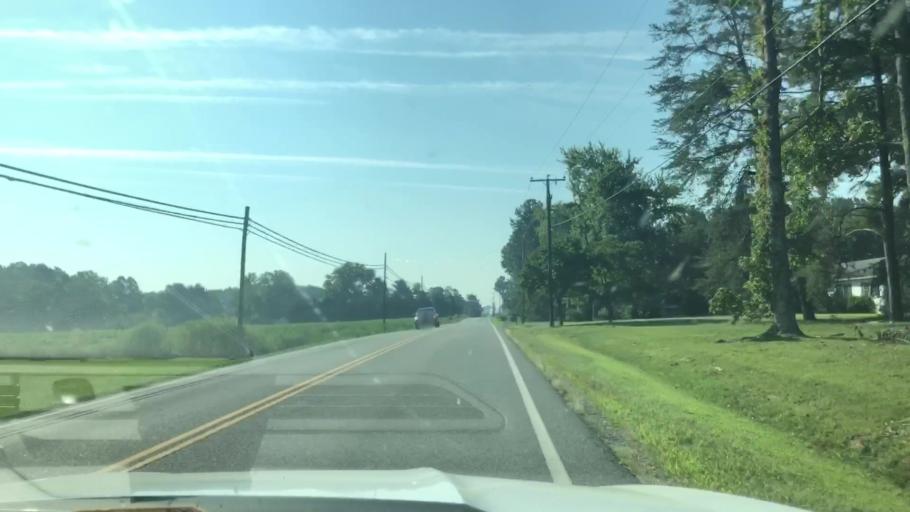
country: US
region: Virginia
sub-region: Richmond County
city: Warsaw
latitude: 37.8956
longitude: -76.6753
